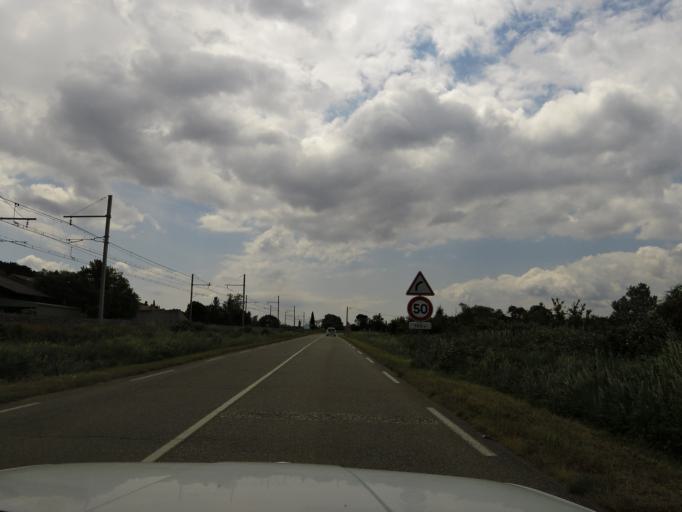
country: FR
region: Rhone-Alpes
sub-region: Departement de la Drome
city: Ancone
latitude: 44.5951
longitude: 4.7506
